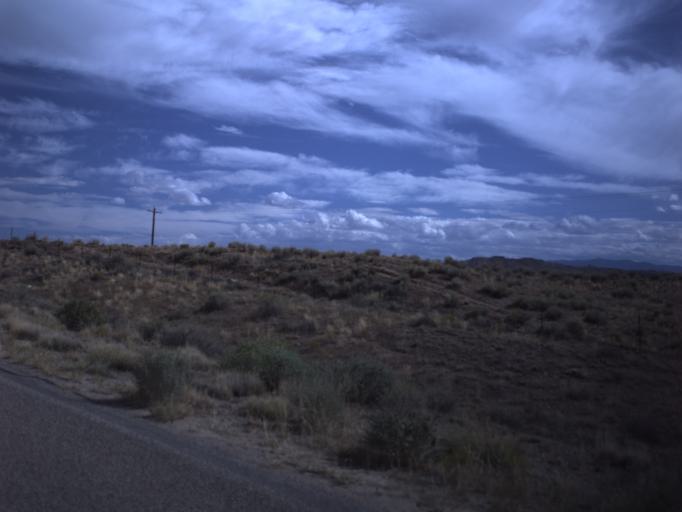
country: US
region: Colorado
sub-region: Montezuma County
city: Towaoc
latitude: 37.2104
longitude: -109.1719
